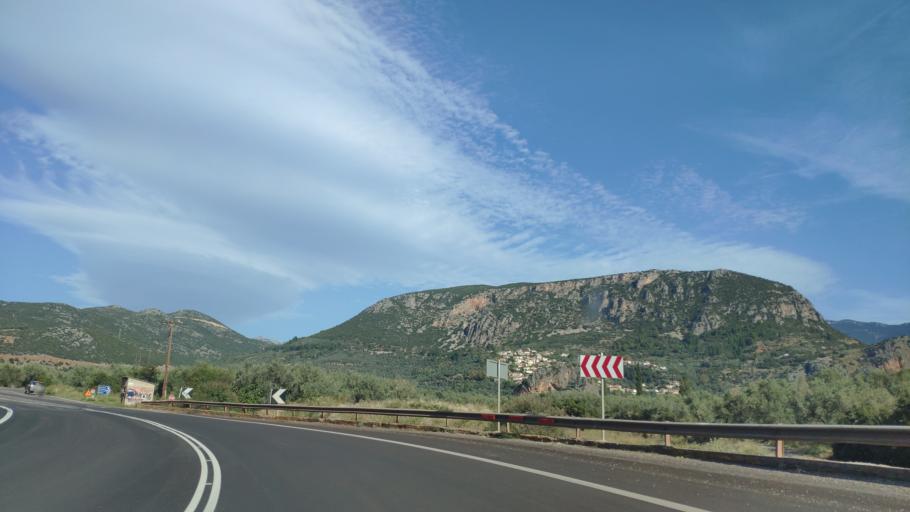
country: GR
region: Central Greece
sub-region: Nomos Fokidos
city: Amfissa
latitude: 38.5361
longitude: 22.4209
